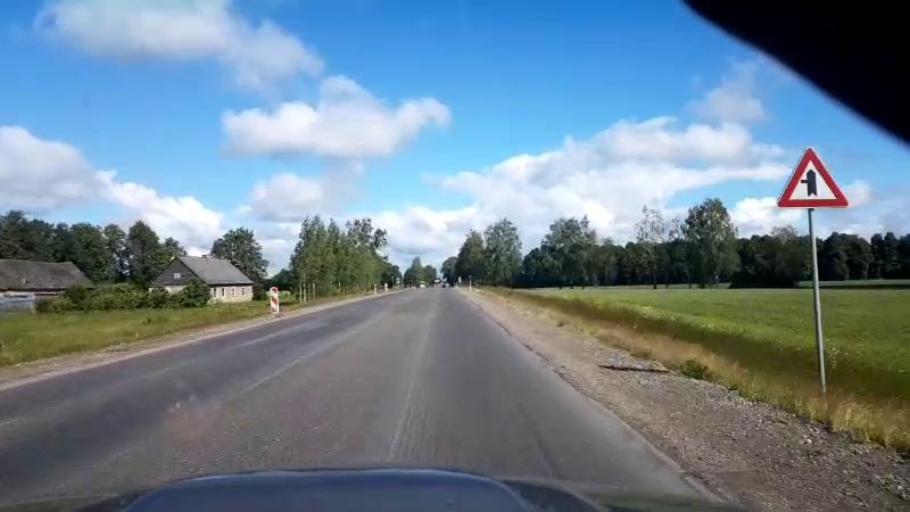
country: LV
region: Bauskas Rajons
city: Bauska
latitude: 56.3774
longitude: 24.2645
